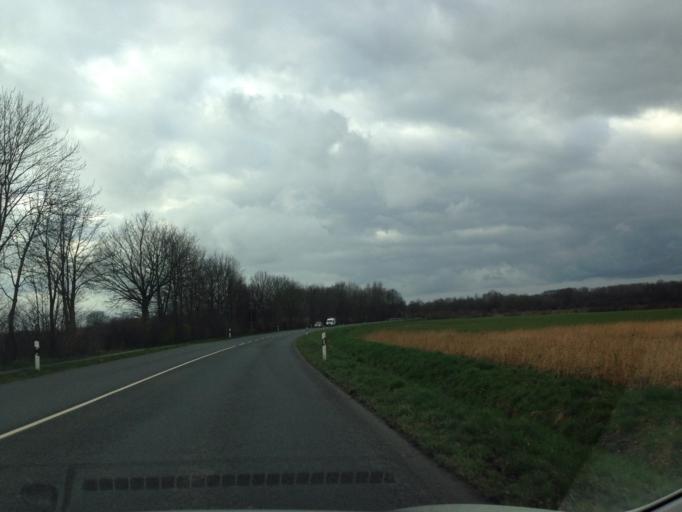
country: DE
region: North Rhine-Westphalia
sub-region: Regierungsbezirk Munster
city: Nordkirchen
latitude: 51.7471
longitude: 7.5272
